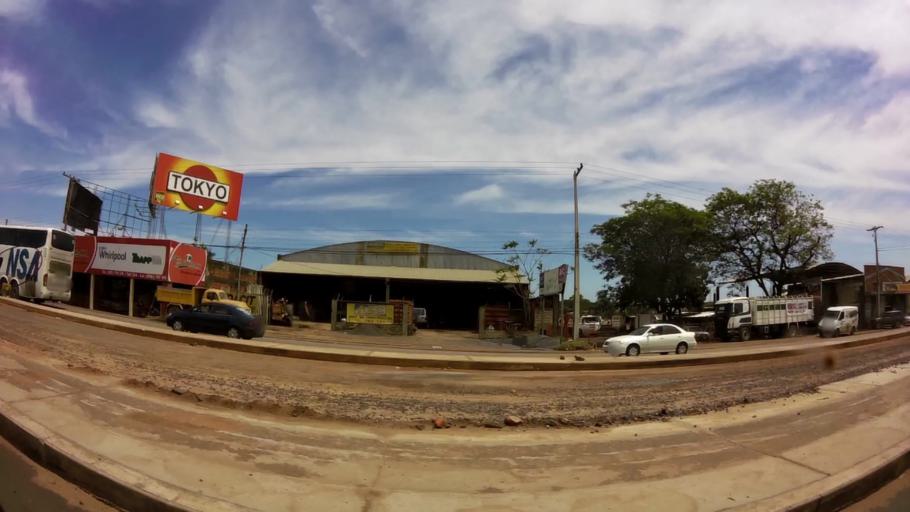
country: PY
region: Central
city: Colonia Mariano Roque Alonso
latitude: -25.2051
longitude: -57.5256
